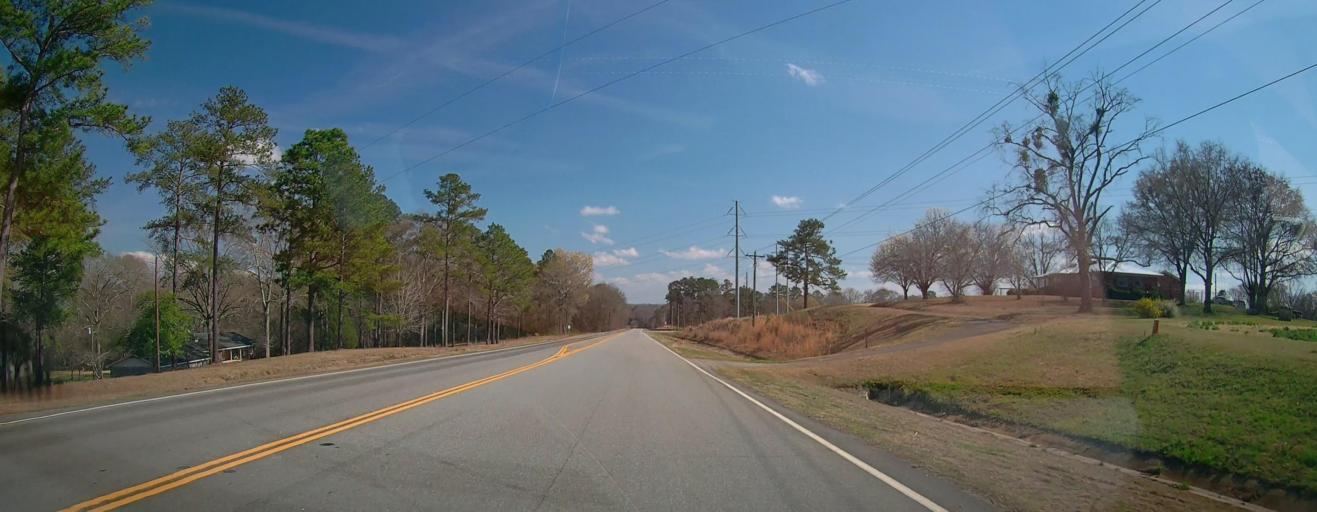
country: US
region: Georgia
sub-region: Wilkinson County
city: Gordon
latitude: 32.9073
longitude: -83.3782
